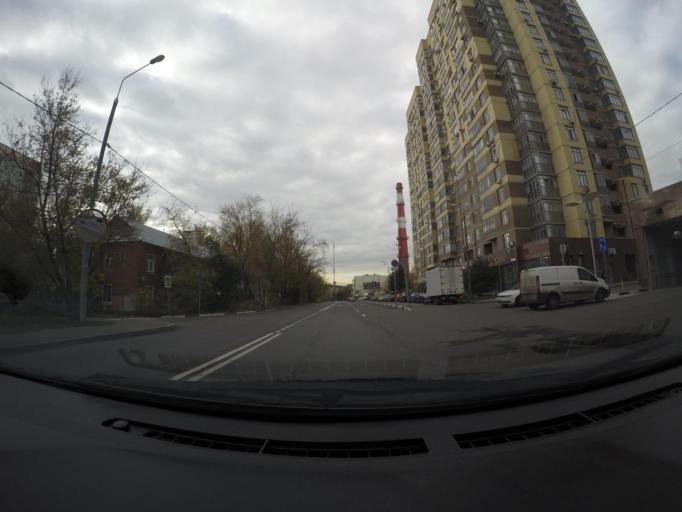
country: RU
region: Moskovskaya
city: Mytishchi
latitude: 55.9153
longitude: 37.7407
